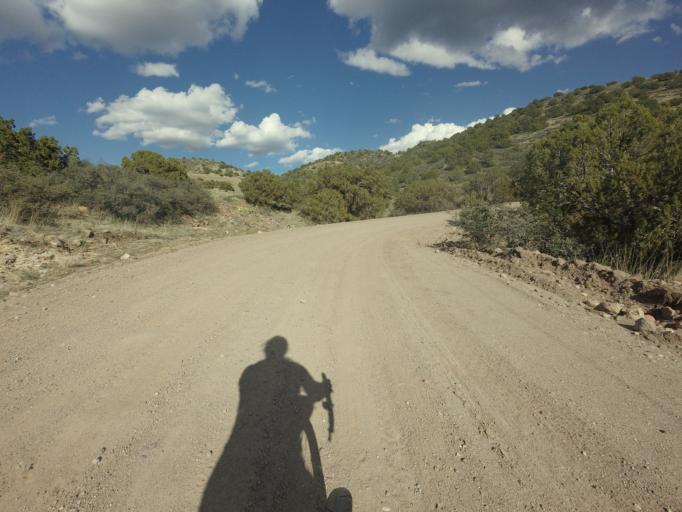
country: US
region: Arizona
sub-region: Yavapai County
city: Camp Verde
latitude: 34.4288
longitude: -111.6758
